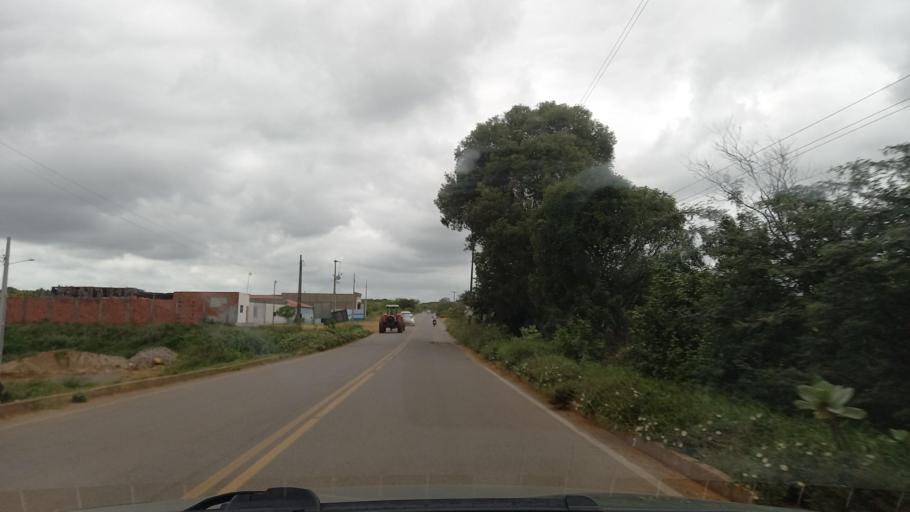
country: BR
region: Sergipe
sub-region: Caninde De Sao Francisco
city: Caninde de Sao Francisco
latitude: -9.6853
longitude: -37.7864
